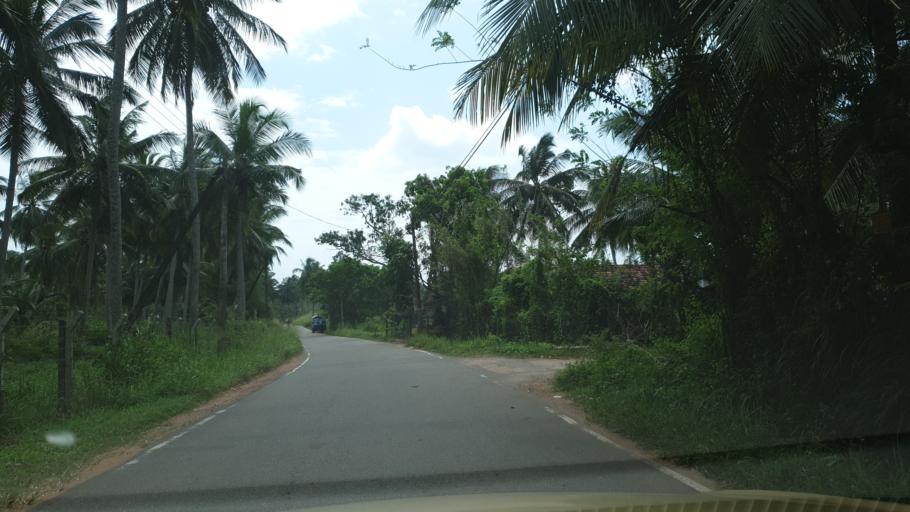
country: LK
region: North Western
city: Kuliyapitiya
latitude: 7.3596
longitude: 79.9673
